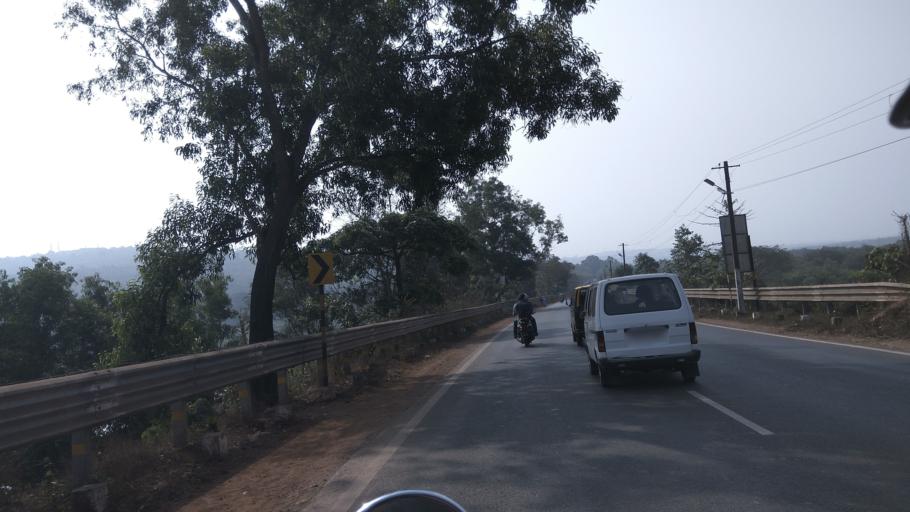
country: IN
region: Goa
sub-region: North Goa
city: Jua
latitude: 15.4891
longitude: 73.9580
